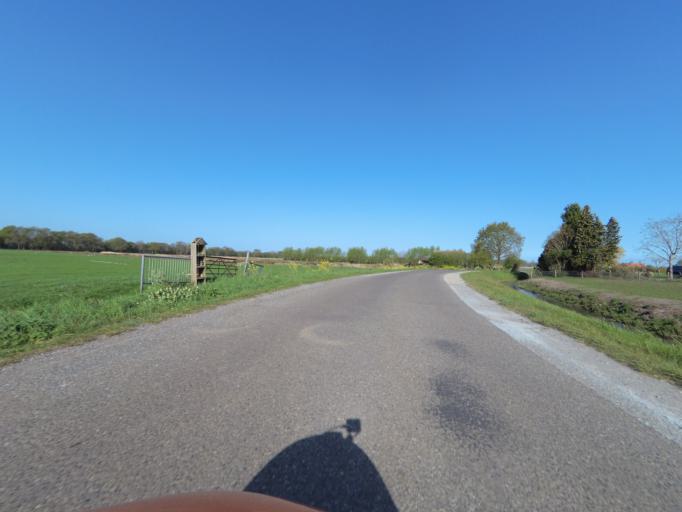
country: NL
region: North Holland
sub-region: Gemeente Naarden
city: Naarden
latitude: 52.3029
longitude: 5.1269
